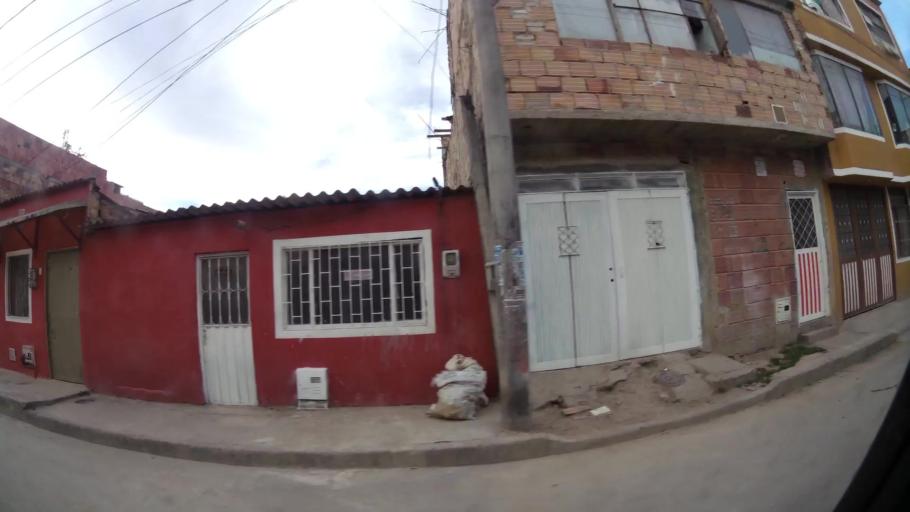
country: CO
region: Cundinamarca
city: Funza
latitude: 4.6915
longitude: -74.1716
